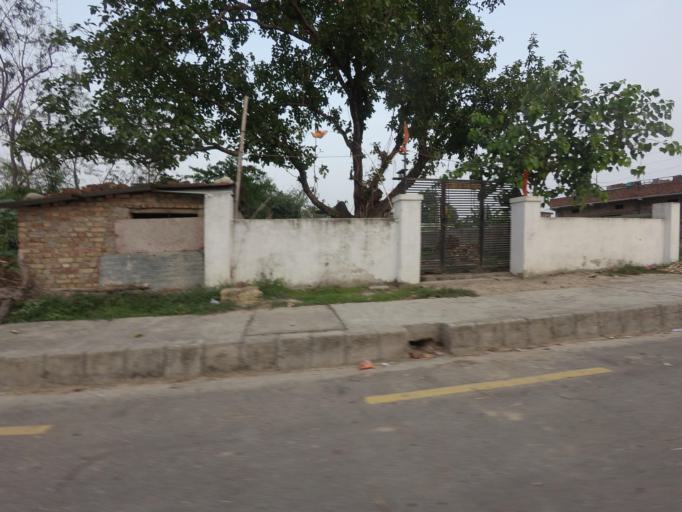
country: NP
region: Western Region
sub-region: Lumbini Zone
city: Bhairahawa
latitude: 27.4945
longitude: 83.4631
